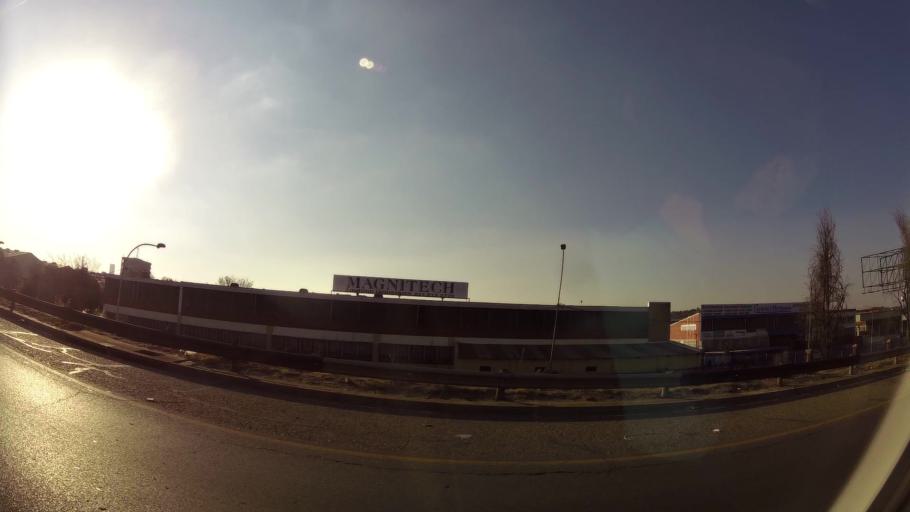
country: ZA
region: Gauteng
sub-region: City of Johannesburg Metropolitan Municipality
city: Johannesburg
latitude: -26.2127
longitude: 28.0807
